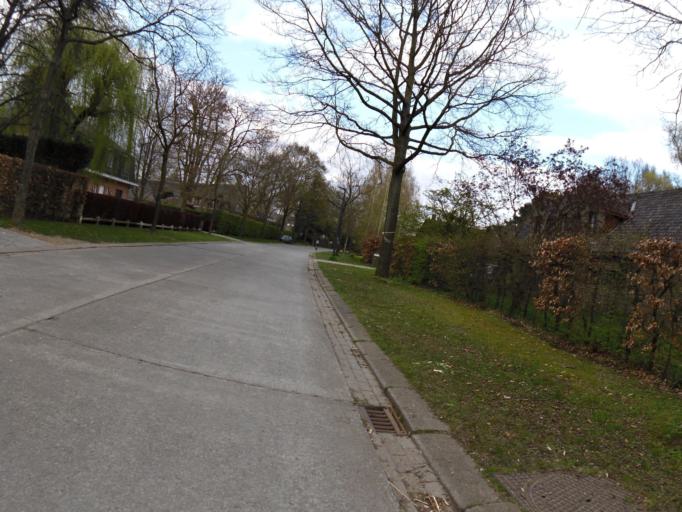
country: BE
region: Flanders
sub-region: Provincie Oost-Vlaanderen
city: Gent
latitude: 51.0136
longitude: 3.6892
